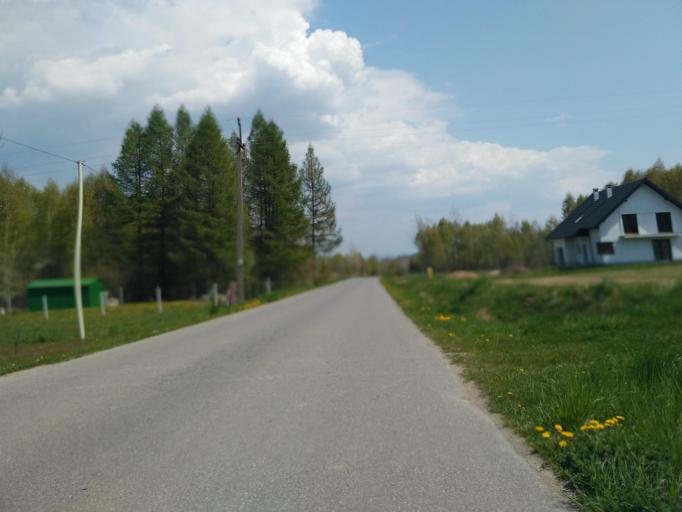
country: PL
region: Subcarpathian Voivodeship
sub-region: Powiat jasielski
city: Debowiec
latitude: 49.6824
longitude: 21.5102
